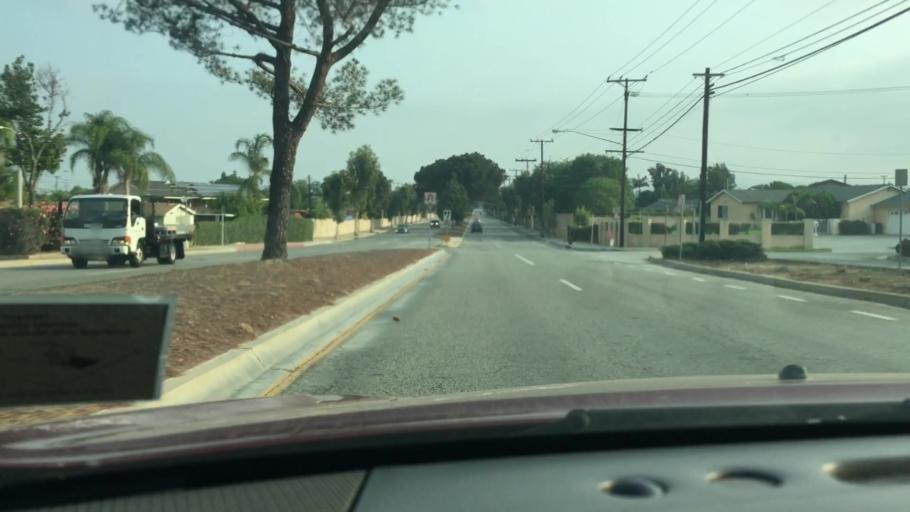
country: US
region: California
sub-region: Los Angeles County
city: La Mirada
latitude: 33.9069
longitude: -118.0292
